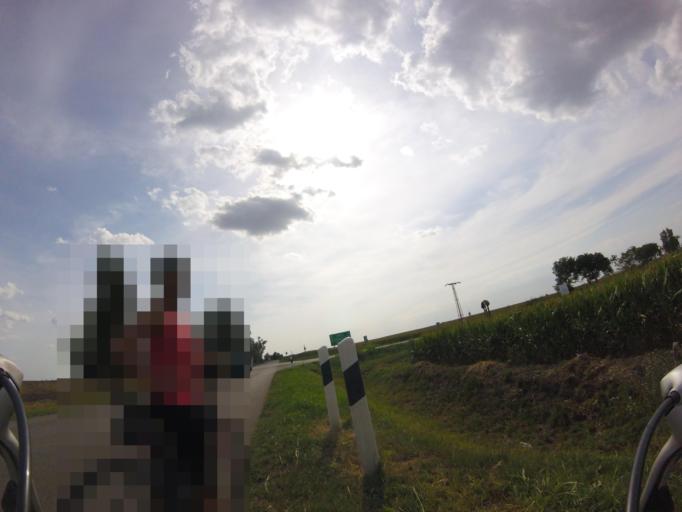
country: HU
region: Bacs-Kiskun
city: Felsoszentivan
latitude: 46.2261
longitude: 19.1663
